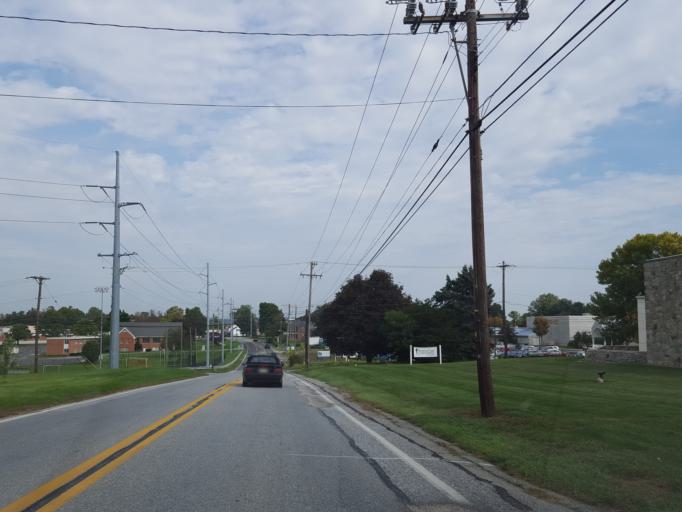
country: US
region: Pennsylvania
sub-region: York County
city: Valley View
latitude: 39.9439
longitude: -76.6934
